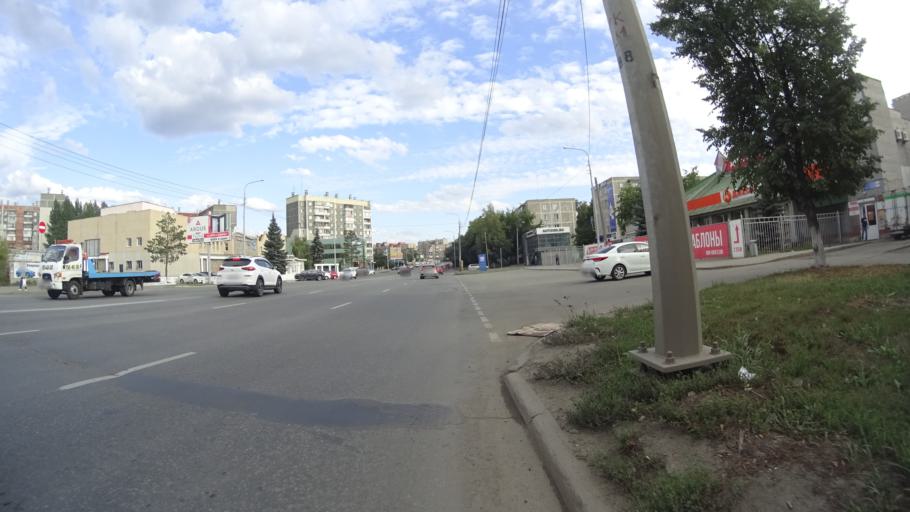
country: RU
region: Chelyabinsk
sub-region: Gorod Chelyabinsk
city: Chelyabinsk
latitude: 55.2003
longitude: 61.3290
